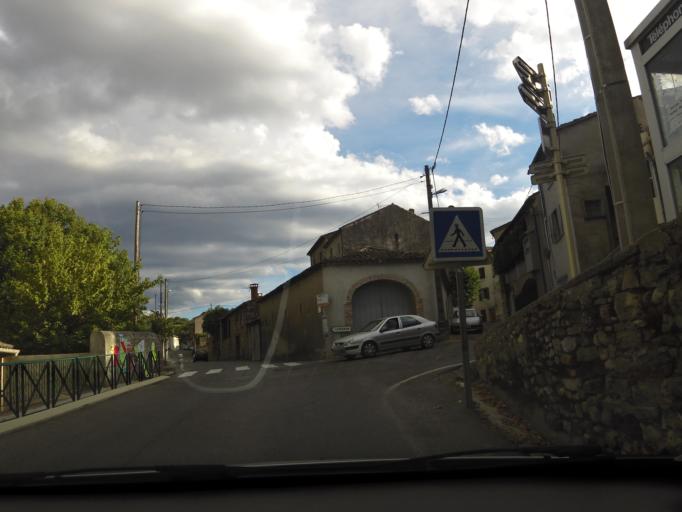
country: FR
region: Languedoc-Roussillon
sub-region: Departement du Gard
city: Lezan
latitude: 44.0133
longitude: 4.0515
